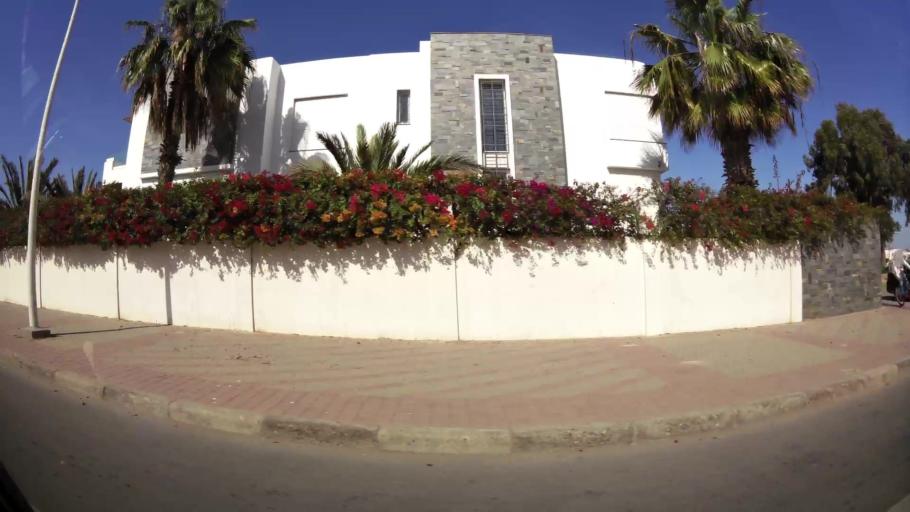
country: MA
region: Oued ed Dahab-Lagouira
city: Dakhla
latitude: 30.3918
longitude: -9.5772
